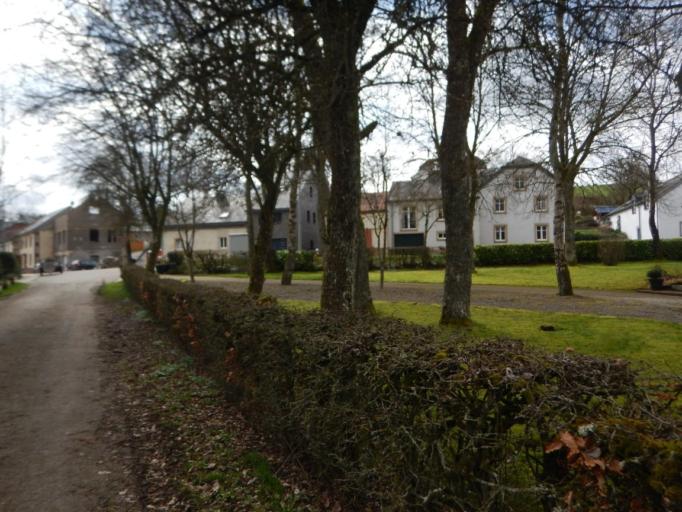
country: LU
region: Diekirch
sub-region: Canton de Wiltz
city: Esch-sur-Sure
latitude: 49.9234
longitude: 5.9018
